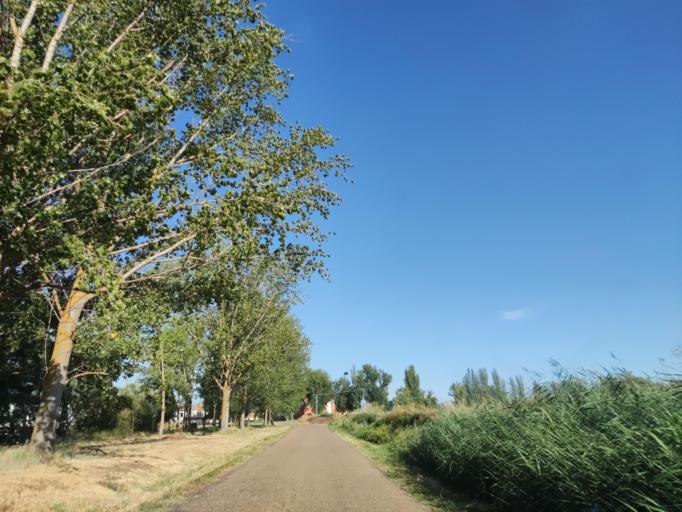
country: ES
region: Castille and Leon
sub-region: Provincia de Zamora
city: Villaralbo
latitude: 41.5021
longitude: -5.6891
